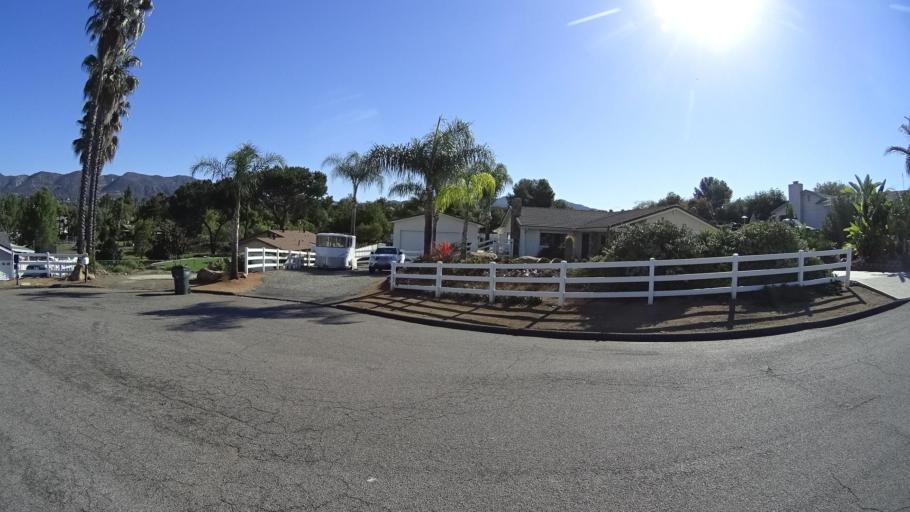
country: US
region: California
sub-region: San Diego County
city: Jamul
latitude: 32.7224
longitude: -116.8713
